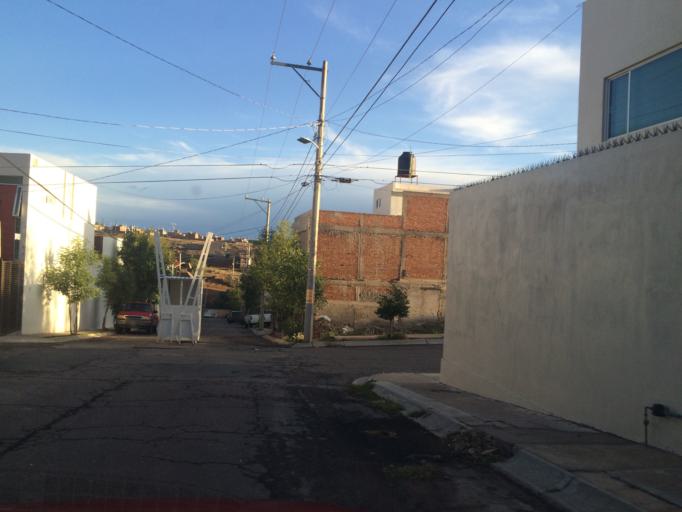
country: MX
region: Zacatecas
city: Zacatecas
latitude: 22.7481
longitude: -102.5835
